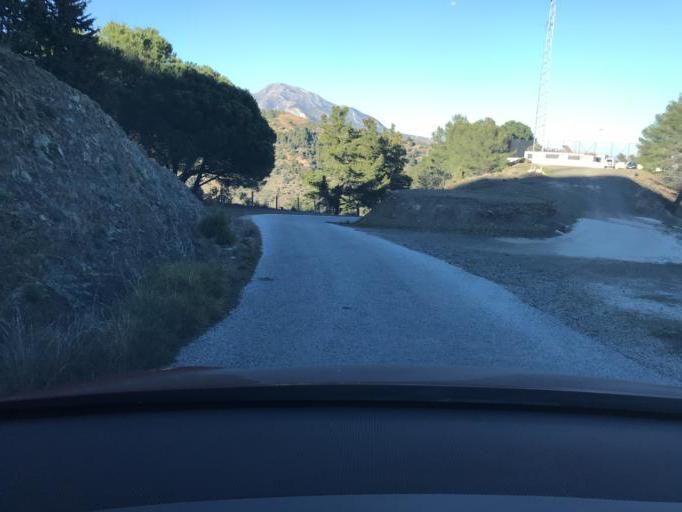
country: ES
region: Andalusia
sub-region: Provincia de Malaga
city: Tolox
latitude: 36.6828
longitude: -4.9143
